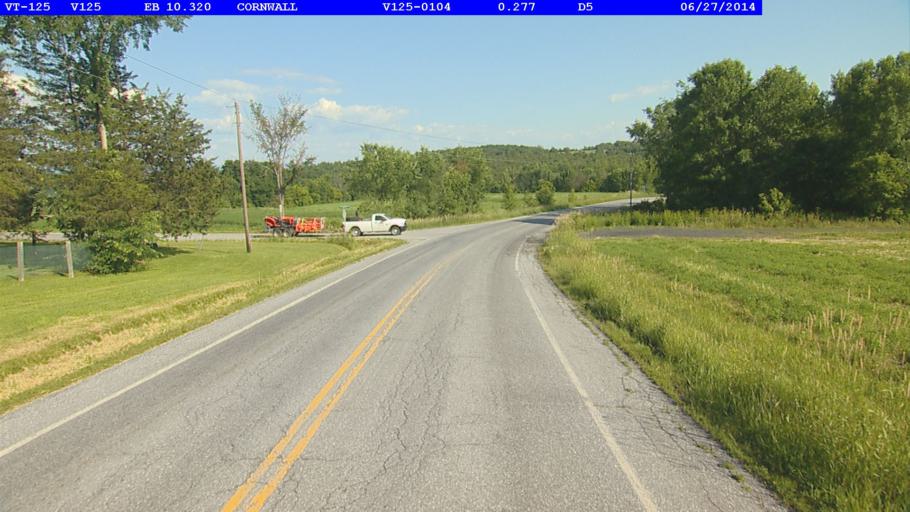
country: US
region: Vermont
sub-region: Addison County
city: Middlebury (village)
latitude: 43.9940
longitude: -73.2531
